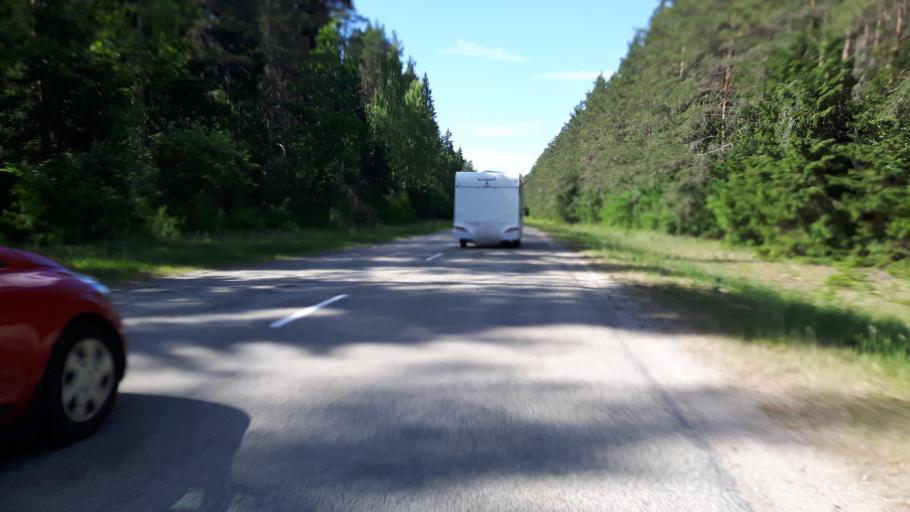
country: LV
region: Talsu Rajons
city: Sabile
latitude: 57.0791
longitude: 22.5293
